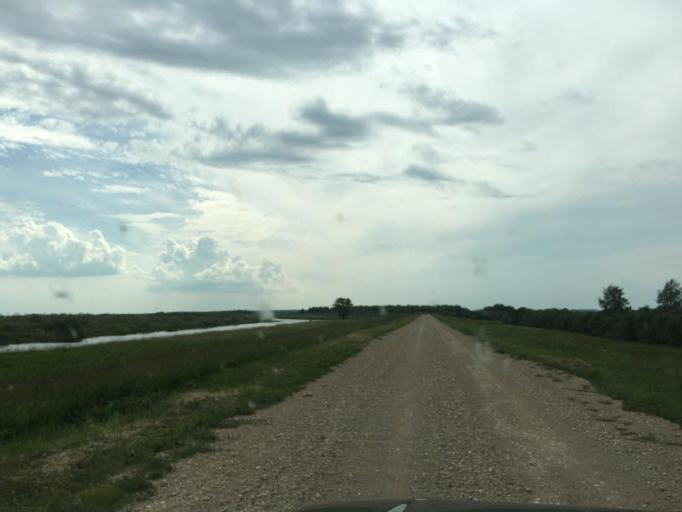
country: LV
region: Lubana
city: Lubana
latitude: 56.8038
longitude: 26.8410
